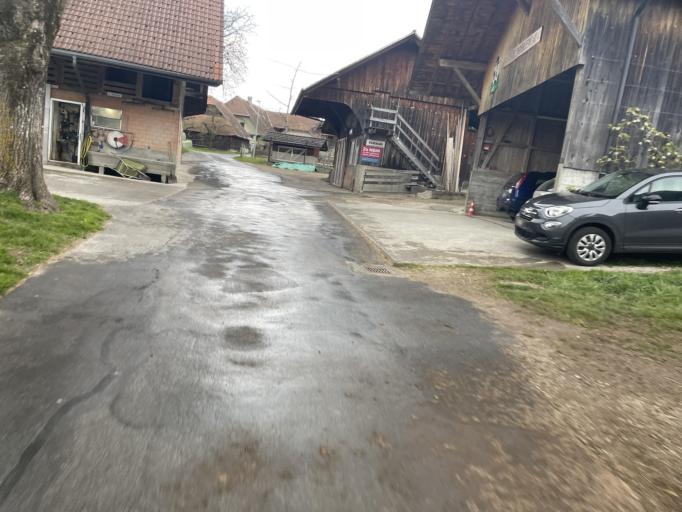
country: CH
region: Bern
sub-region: Bern-Mittelland District
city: Taegertschi
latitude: 46.9005
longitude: 7.5948
